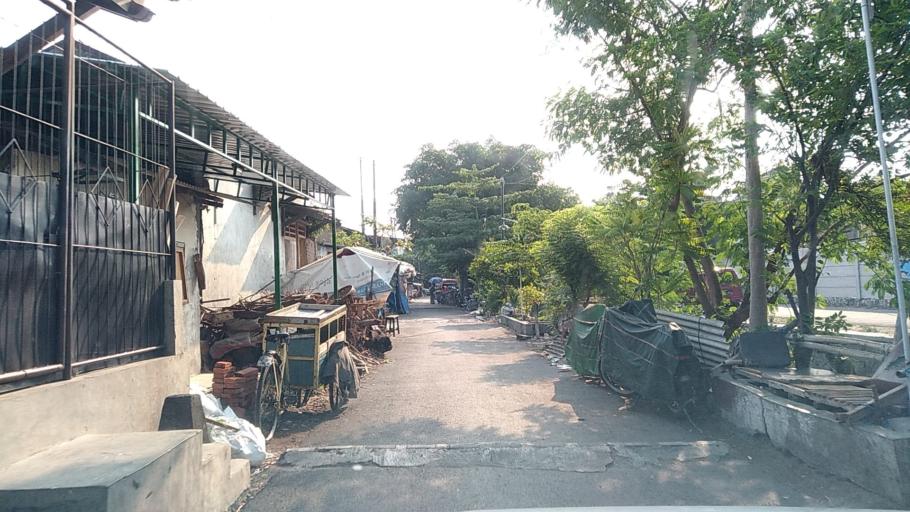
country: ID
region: Central Java
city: Semarang
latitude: -6.9809
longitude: 110.4202
